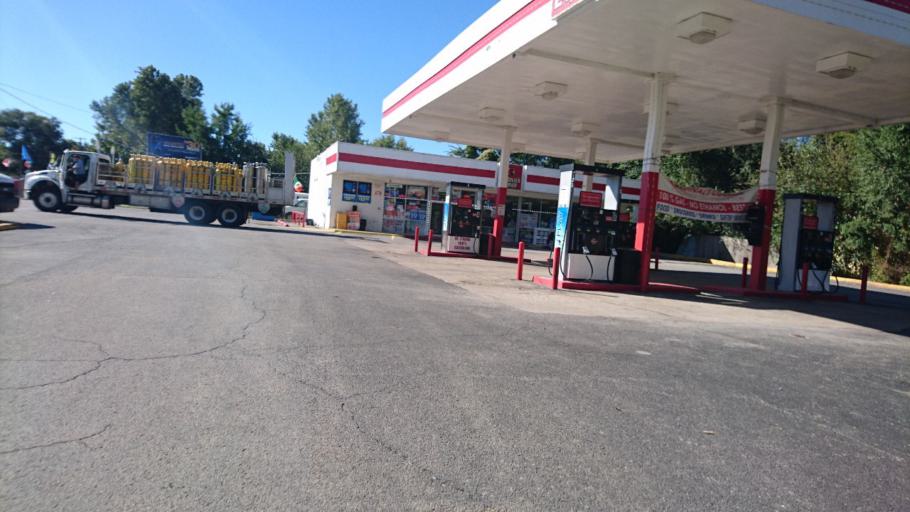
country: US
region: Oklahoma
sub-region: Rogers County
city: Catoosa
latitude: 36.1479
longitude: -95.8158
